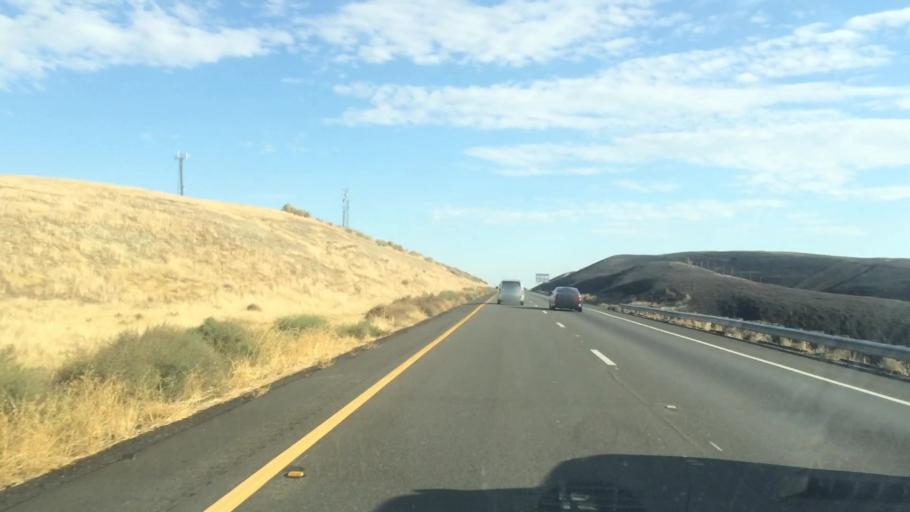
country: US
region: California
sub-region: Kings County
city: Kettleman City
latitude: 35.9901
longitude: -119.9692
